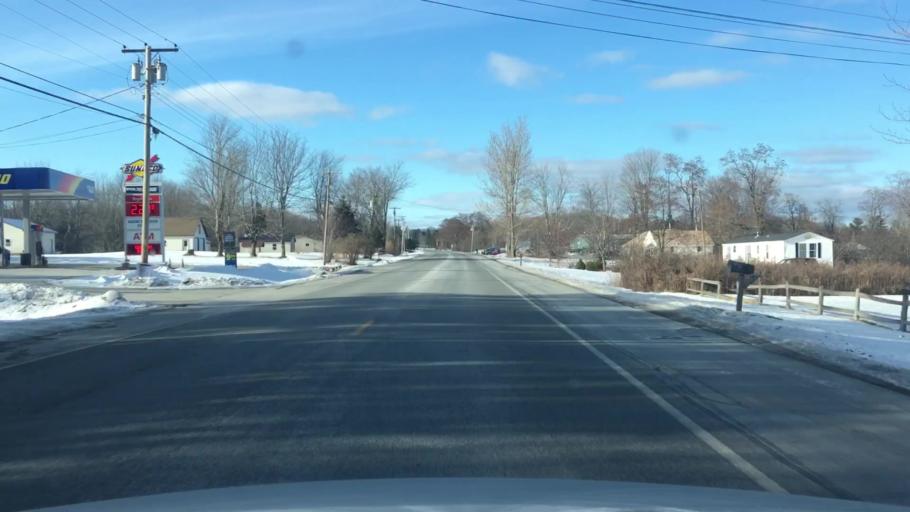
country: US
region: Maine
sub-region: Penobscot County
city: Eddington
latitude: 44.8233
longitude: -68.6516
